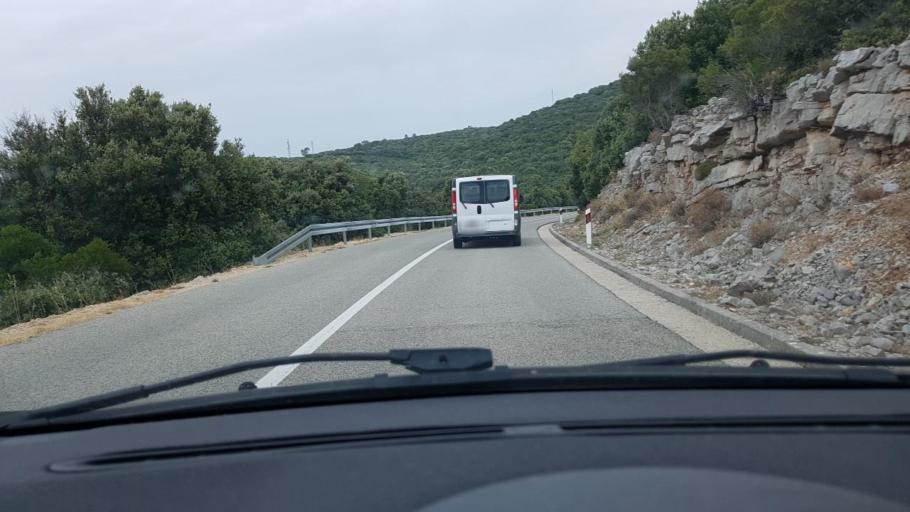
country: HR
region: Dubrovacko-Neretvanska
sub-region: Grad Korcula
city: Zrnovo
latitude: 42.9414
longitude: 17.0072
